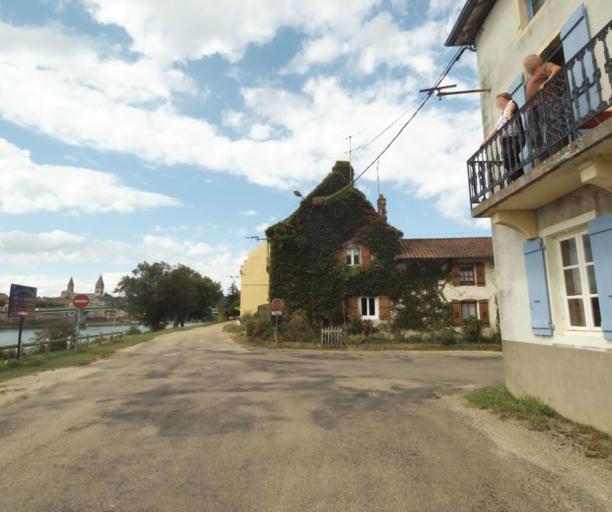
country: FR
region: Bourgogne
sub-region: Departement de Saone-et-Loire
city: Tournus
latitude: 46.5628
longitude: 4.9160
